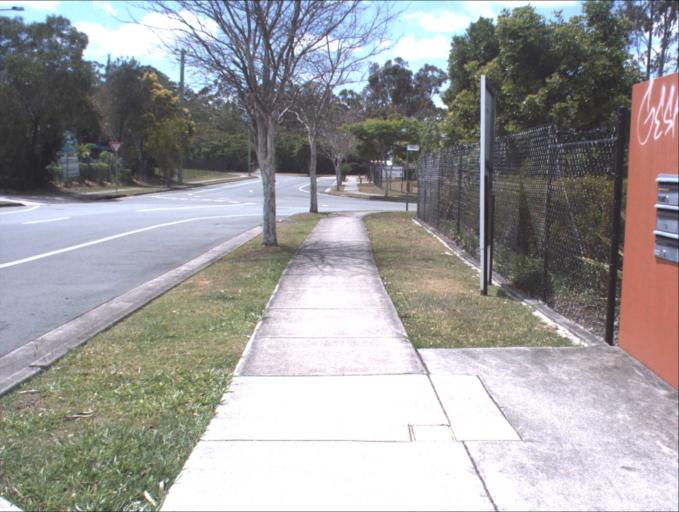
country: AU
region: Queensland
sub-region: Logan
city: Slacks Creek
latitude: -27.6544
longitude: 153.1658
